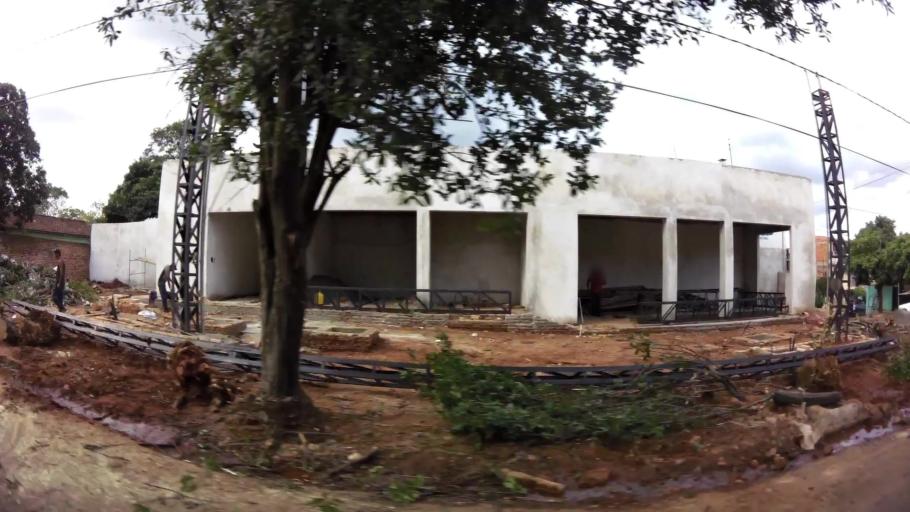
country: PY
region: Central
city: Villa Elisa
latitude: -25.3477
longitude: -57.5642
